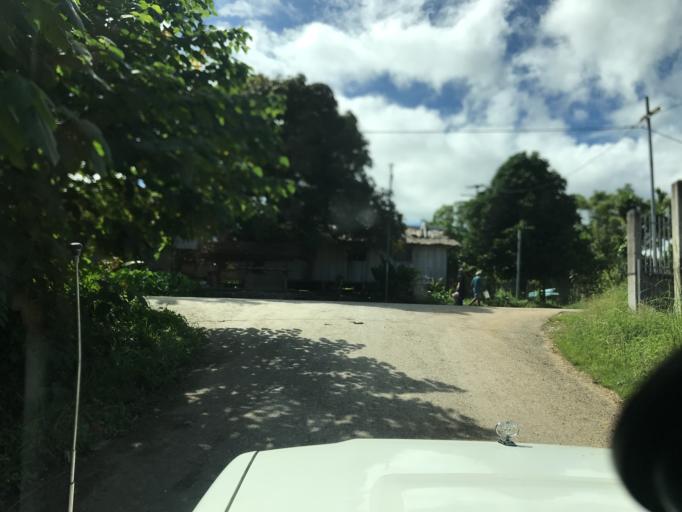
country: SB
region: Malaita
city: Auki
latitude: -8.7650
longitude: 160.6967
